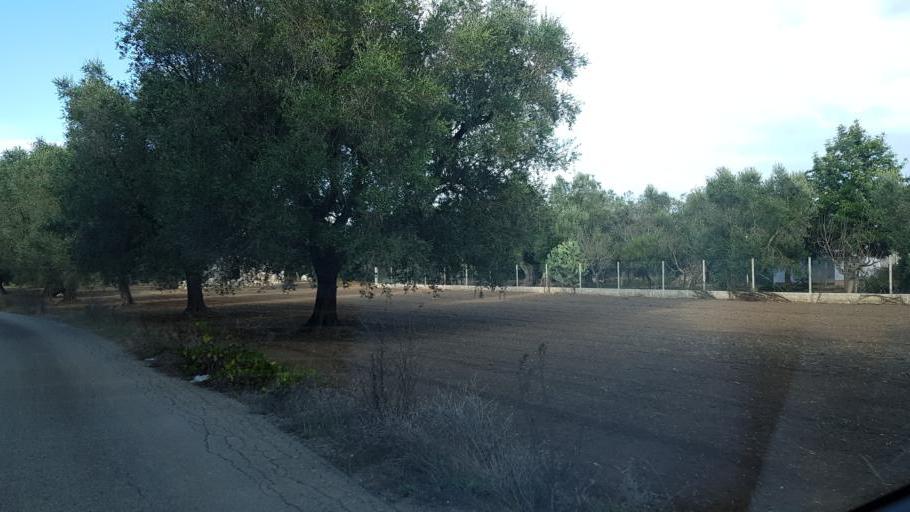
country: IT
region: Apulia
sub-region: Provincia di Brindisi
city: Oria
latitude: 40.5058
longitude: 17.6719
